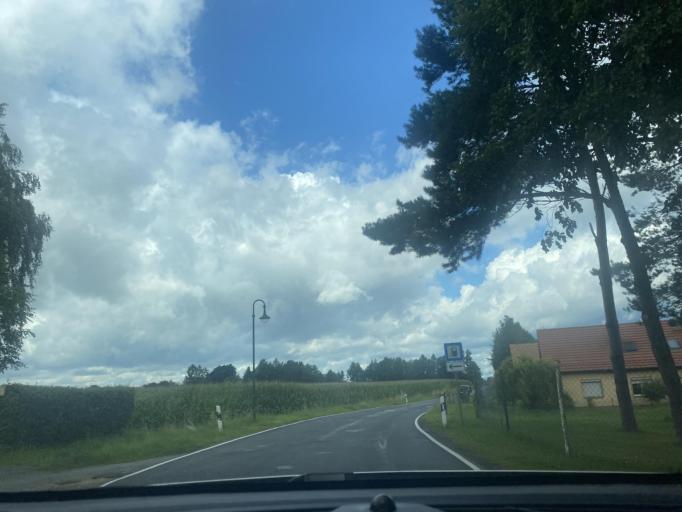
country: DE
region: Saxony
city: Sohland am Rotstein
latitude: 51.1317
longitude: 14.7733
